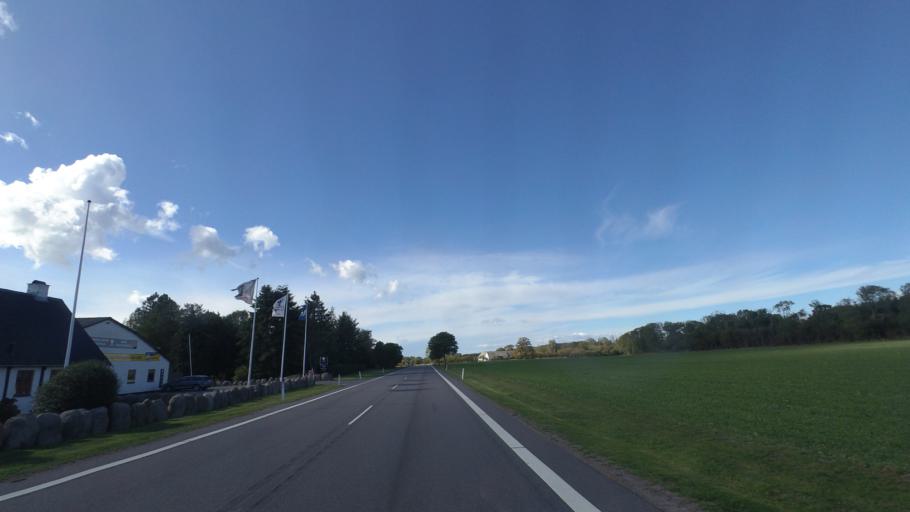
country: DK
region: Capital Region
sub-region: Bornholm Kommune
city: Ronne
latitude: 55.0723
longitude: 14.8045
